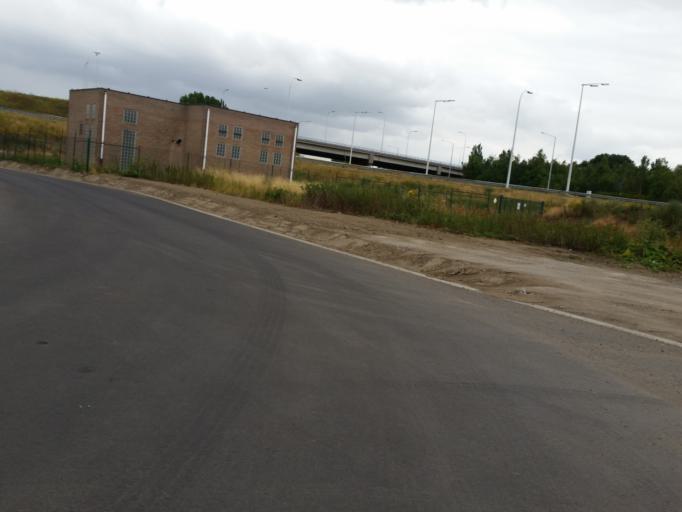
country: BE
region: Flanders
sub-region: Provincie Antwerpen
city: Mechelen
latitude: 51.0499
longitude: 4.4553
